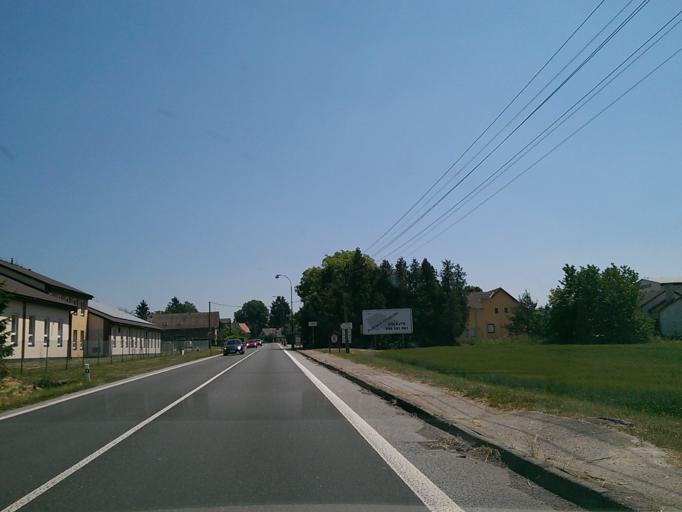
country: CZ
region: Liberecky
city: Rovensko pod Troskami
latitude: 50.5006
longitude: 15.2939
